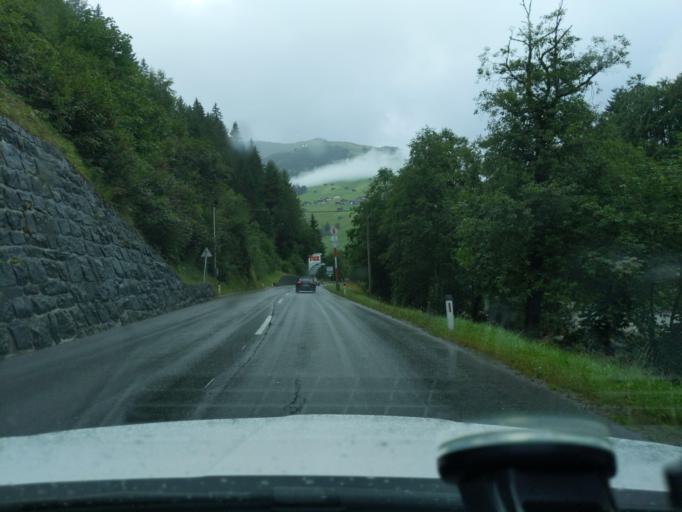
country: AT
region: Tyrol
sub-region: Politischer Bezirk Schwaz
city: Schwendau
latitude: 47.1609
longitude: 11.7491
